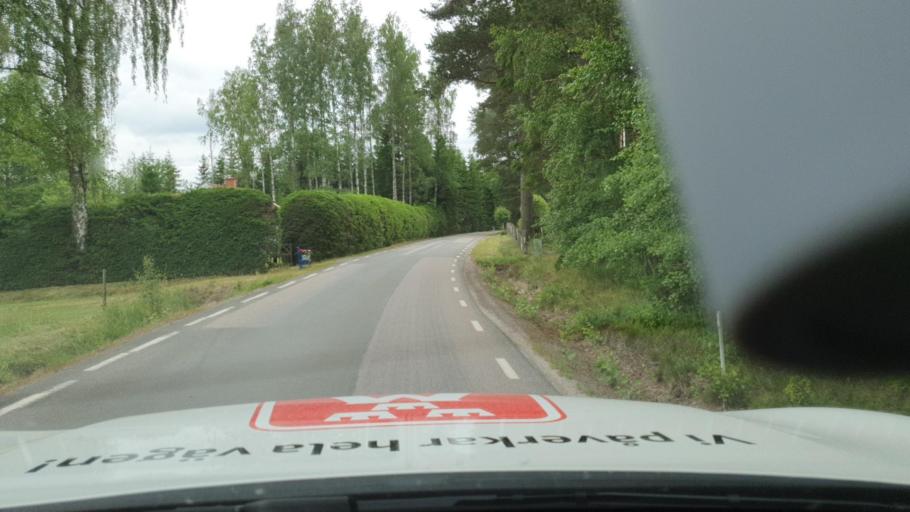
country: SE
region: Vaestra Goetaland
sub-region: Tidaholms Kommun
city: Olofstorp
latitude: 58.2493
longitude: 14.0985
